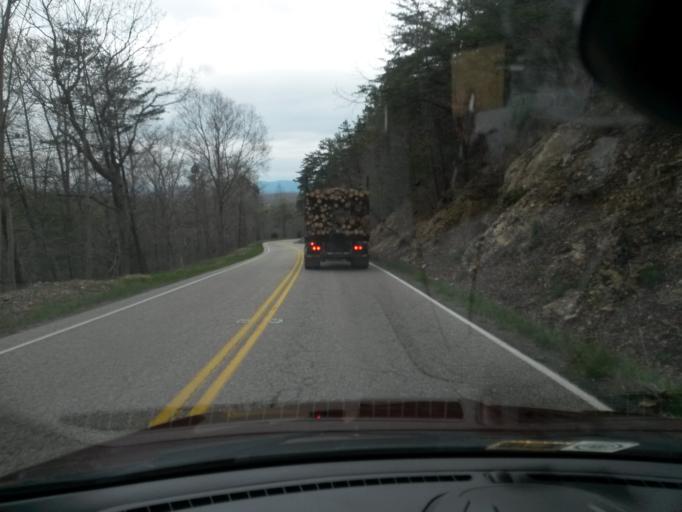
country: US
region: Virginia
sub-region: City of Buena Vista
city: Buena Vista
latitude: 37.7372
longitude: -79.3312
